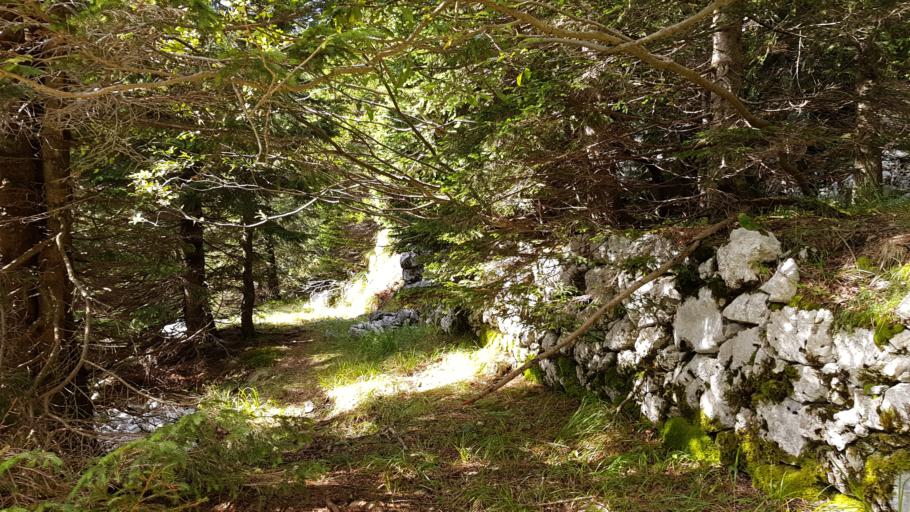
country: SI
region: Kobarid
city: Kobarid
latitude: 46.2898
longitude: 13.6057
